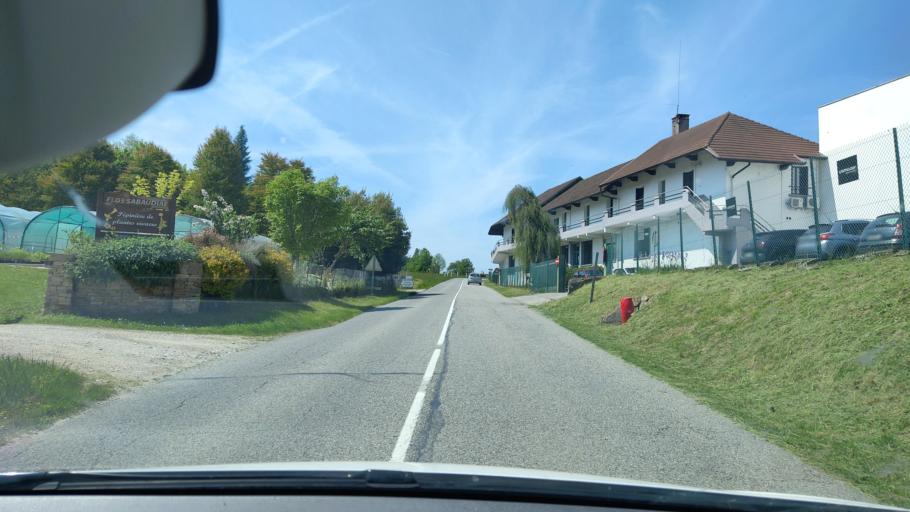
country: FR
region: Rhone-Alpes
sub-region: Departement de la Savoie
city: La Bridoire
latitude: 45.5290
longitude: 5.7231
